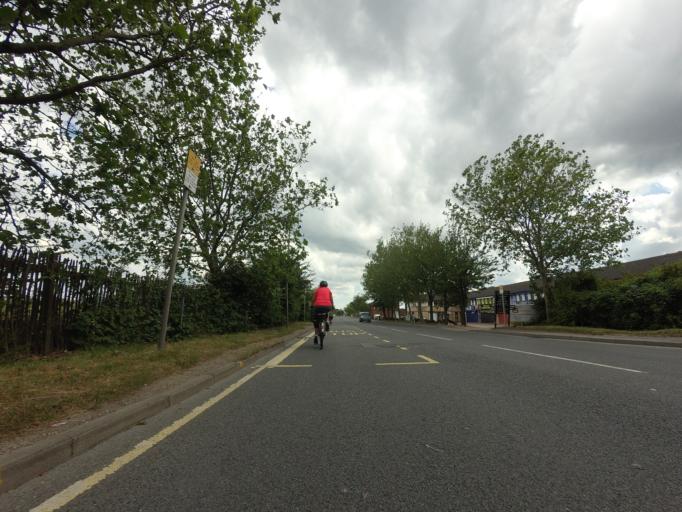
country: GB
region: England
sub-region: Medway
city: Rochester
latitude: 51.3993
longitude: 0.5152
